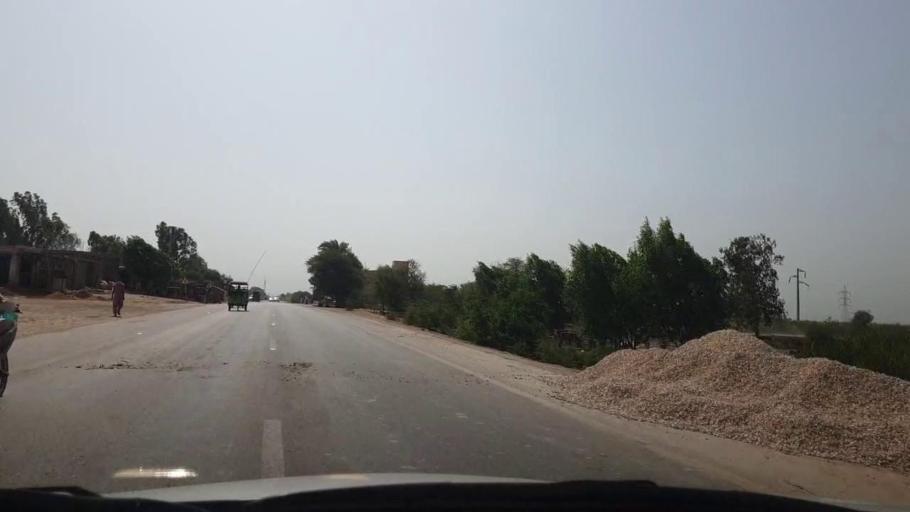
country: PK
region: Sindh
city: Tando Muhammad Khan
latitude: 25.1027
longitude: 68.5882
